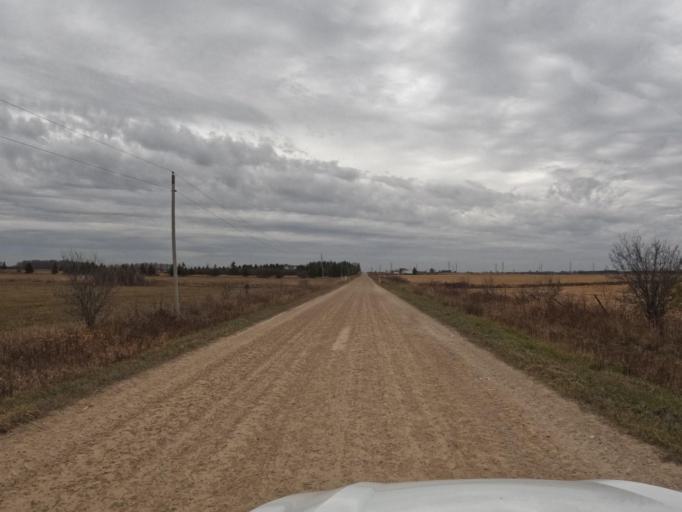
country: CA
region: Ontario
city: Shelburne
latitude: 44.0100
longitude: -80.3893
